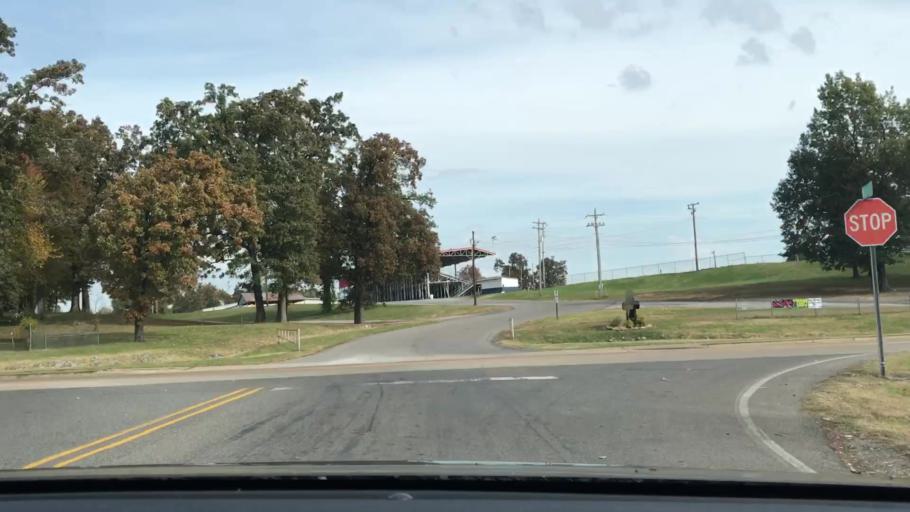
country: US
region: Kentucky
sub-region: Graves County
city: Mayfield
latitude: 36.7524
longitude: -88.6515
